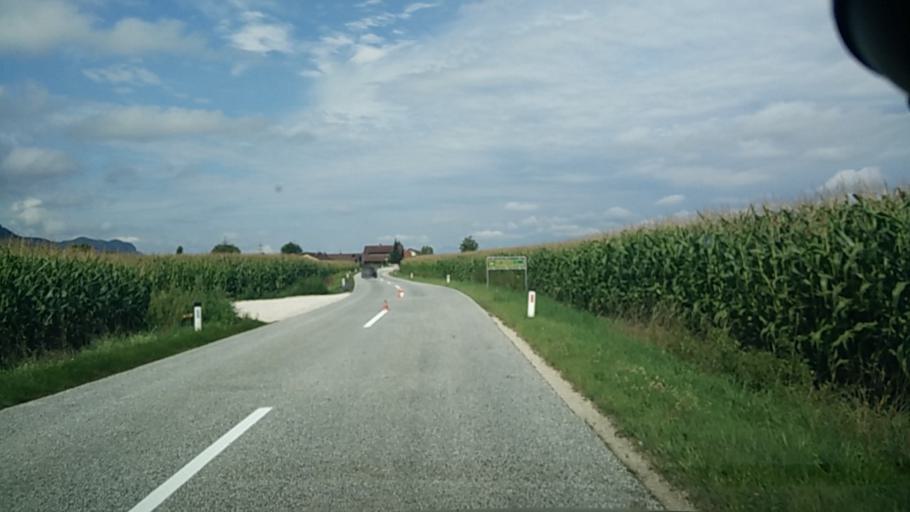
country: AT
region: Carinthia
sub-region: Politischer Bezirk Klagenfurt Land
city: Grafenstein
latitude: 46.6128
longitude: 14.4917
